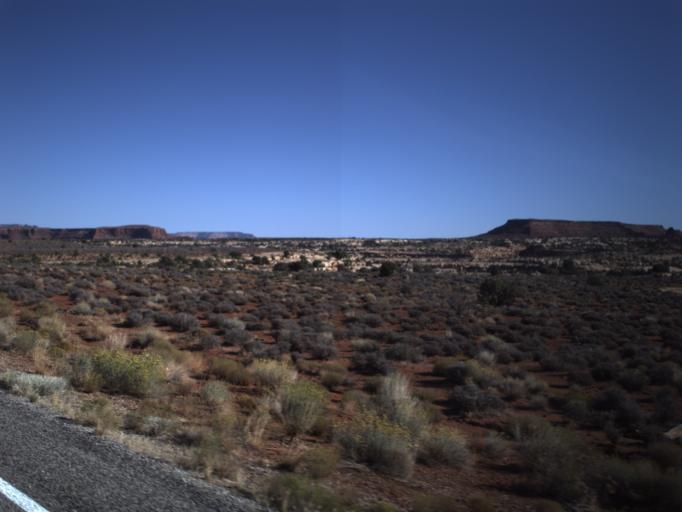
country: US
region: Utah
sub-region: San Juan County
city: Blanding
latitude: 37.7730
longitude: -110.2880
